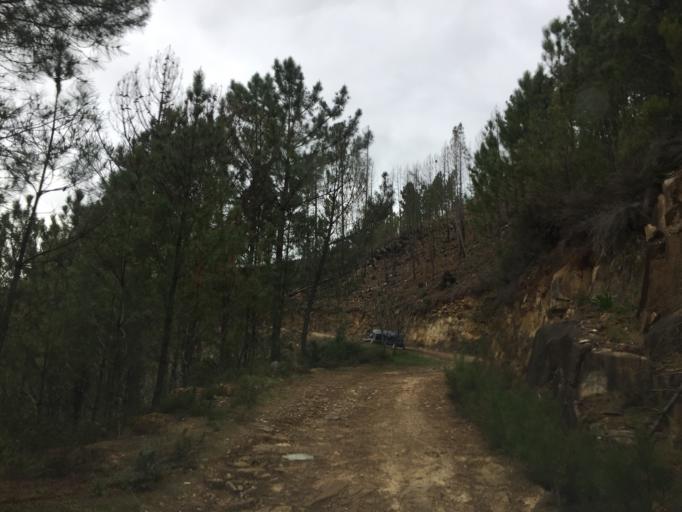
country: PT
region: Guarda
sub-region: Seia
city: Seia
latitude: 40.3186
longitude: -7.7304
